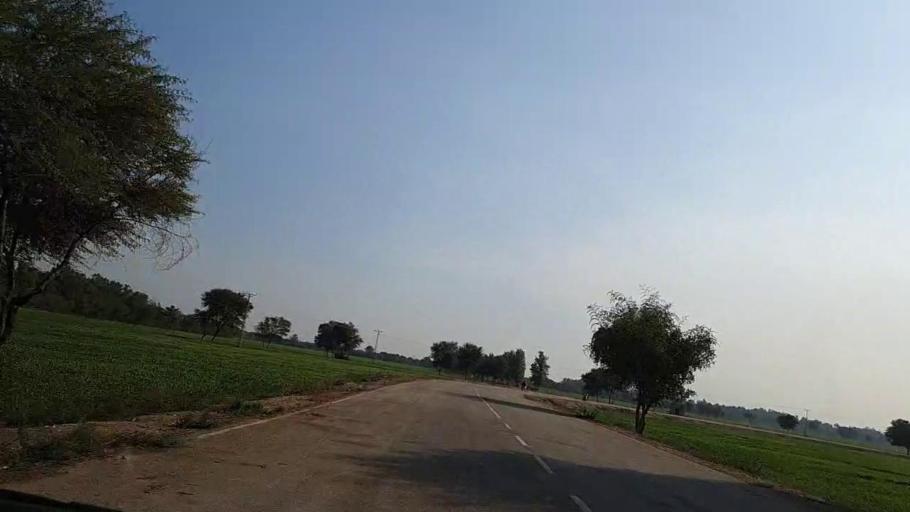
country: PK
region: Sindh
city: Sakrand
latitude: 26.1190
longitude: 68.2494
